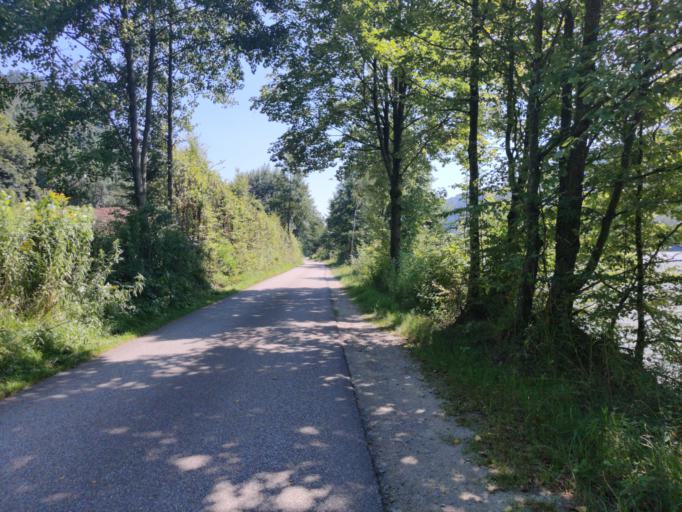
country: AT
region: Upper Austria
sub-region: Politischer Bezirk Rohrbach
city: Pfarrkirchen im Muehlkreis
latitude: 48.4559
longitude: 13.8208
